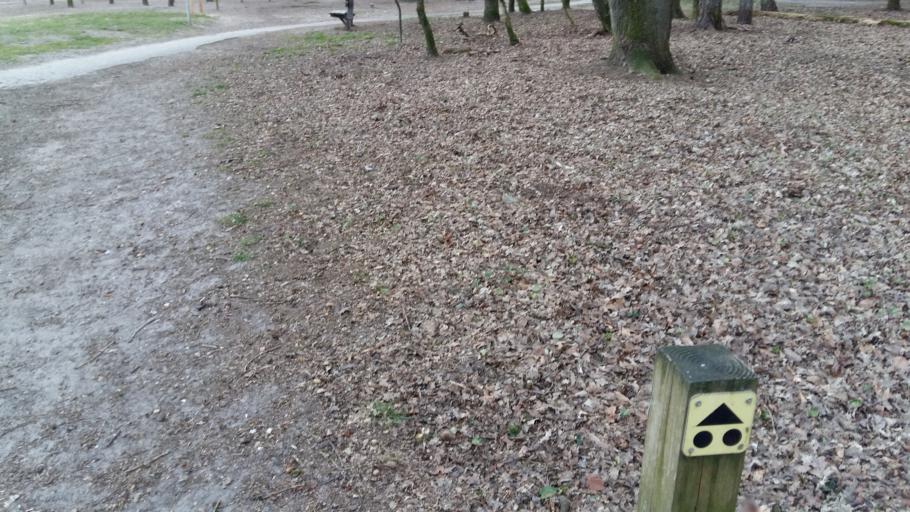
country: NL
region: Gelderland
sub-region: Gemeente Ede
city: Ede
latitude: 52.0437
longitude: 5.6938
